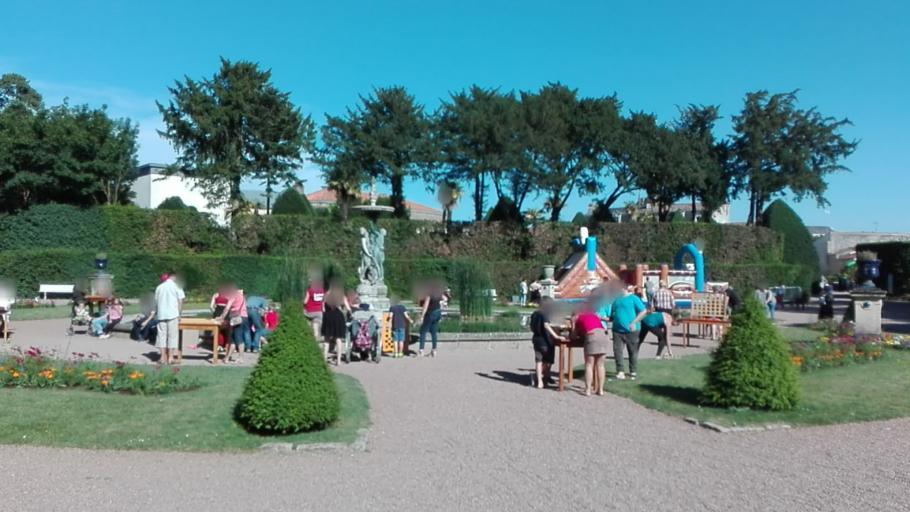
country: FR
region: Pays de la Loire
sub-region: Departement de la Vendee
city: Lucon
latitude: 46.4562
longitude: -1.1705
